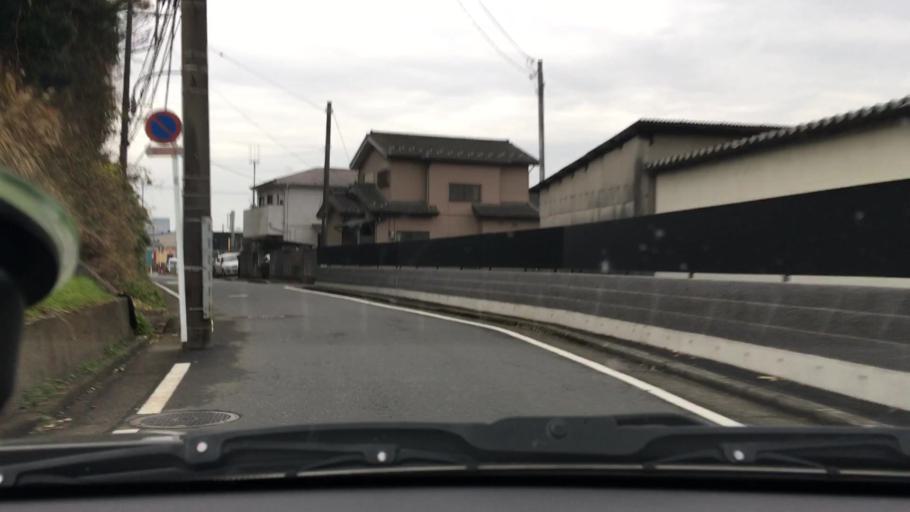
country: JP
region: Kanagawa
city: Yokohama
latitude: 35.5201
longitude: 139.6036
